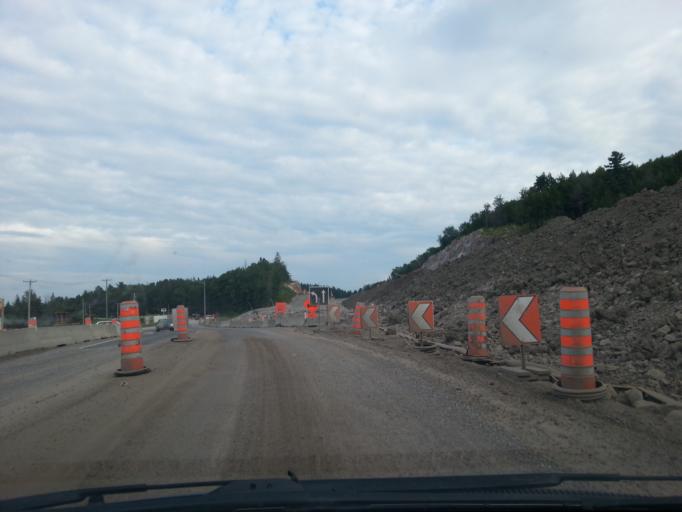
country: CA
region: Quebec
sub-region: Outaouais
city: Wakefield
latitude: 45.6256
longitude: -75.9357
